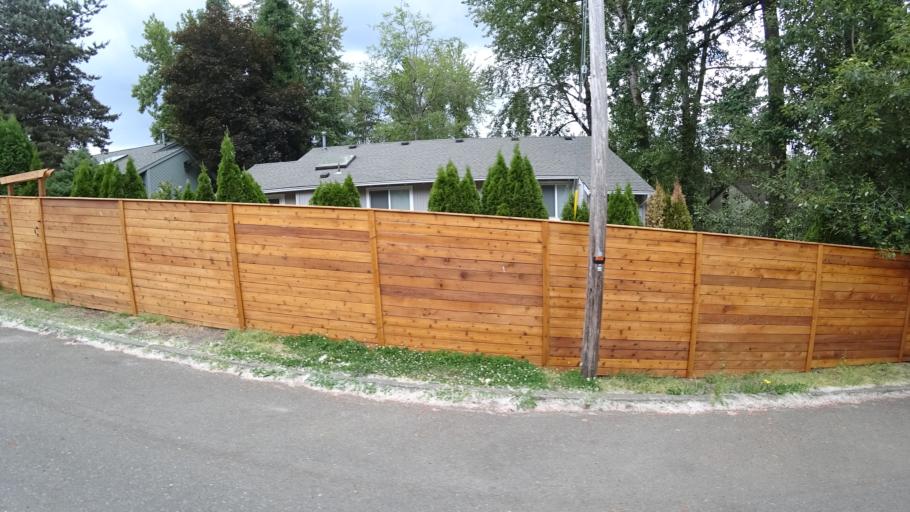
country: US
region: Oregon
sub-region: Clackamas County
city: Lake Oswego
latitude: 45.4518
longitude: -122.7063
